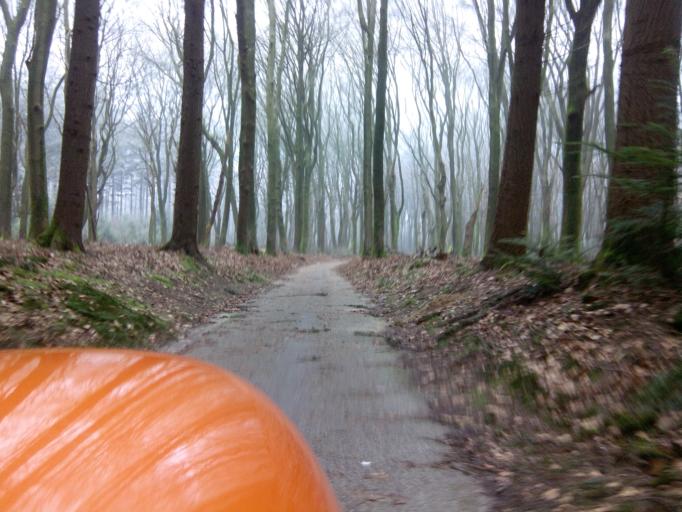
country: NL
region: Gelderland
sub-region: Gemeente Barneveld
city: Garderen
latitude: 52.2603
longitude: 5.6842
